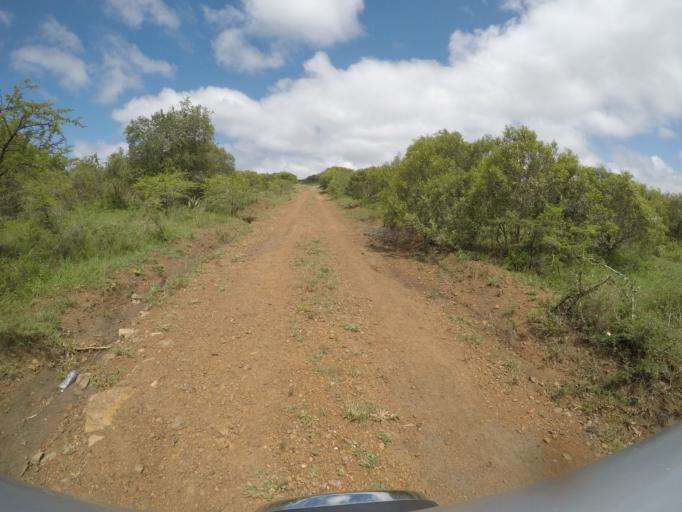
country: ZA
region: KwaZulu-Natal
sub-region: uThungulu District Municipality
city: Empangeni
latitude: -28.5730
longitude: 31.8300
